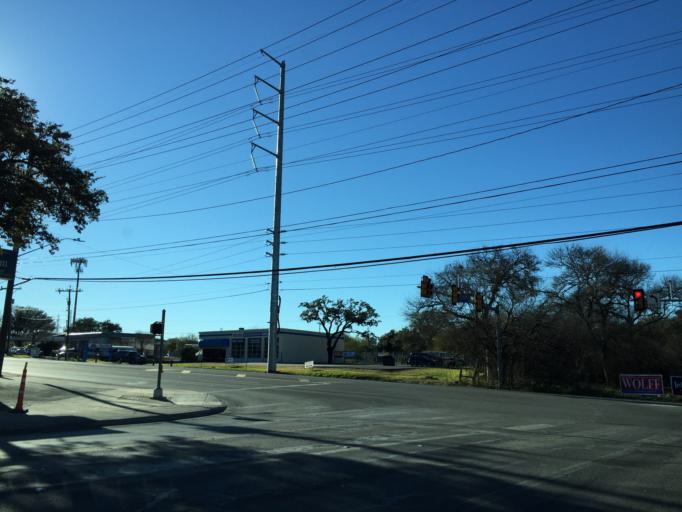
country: US
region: Texas
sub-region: Bexar County
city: Castle Hills
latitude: 29.5542
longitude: -98.5004
